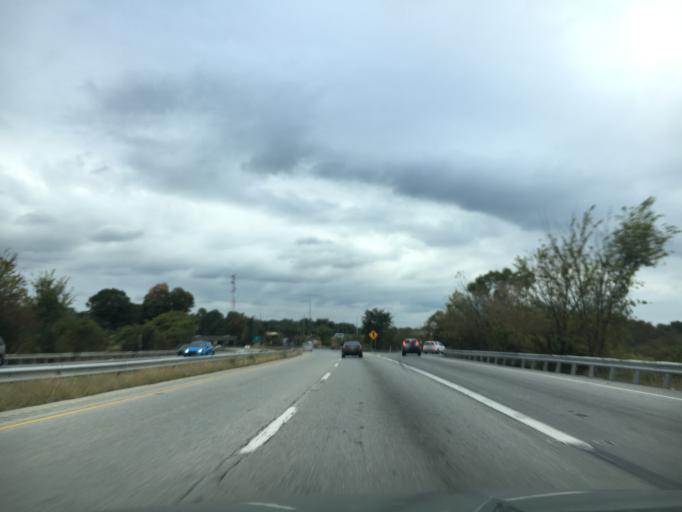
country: US
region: Pennsylvania
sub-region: Chester County
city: Caln
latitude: 40.0061
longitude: -75.7853
